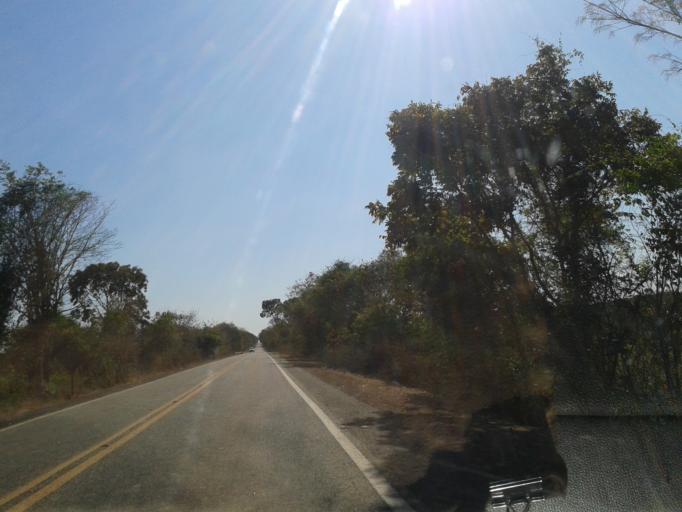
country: BR
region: Goias
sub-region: Mozarlandia
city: Mozarlandia
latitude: -14.4915
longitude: -50.4825
